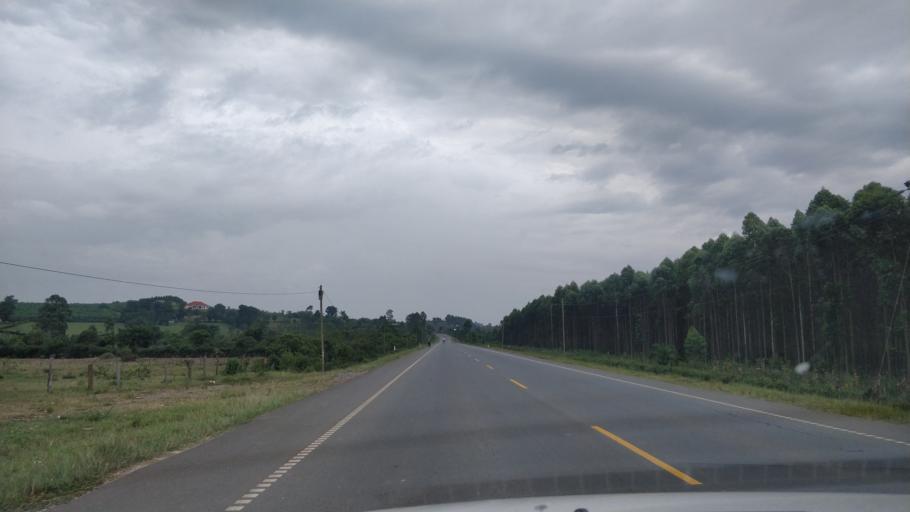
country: UG
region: Western Region
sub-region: Sheema District
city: Kibingo
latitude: -0.6570
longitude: 30.4738
